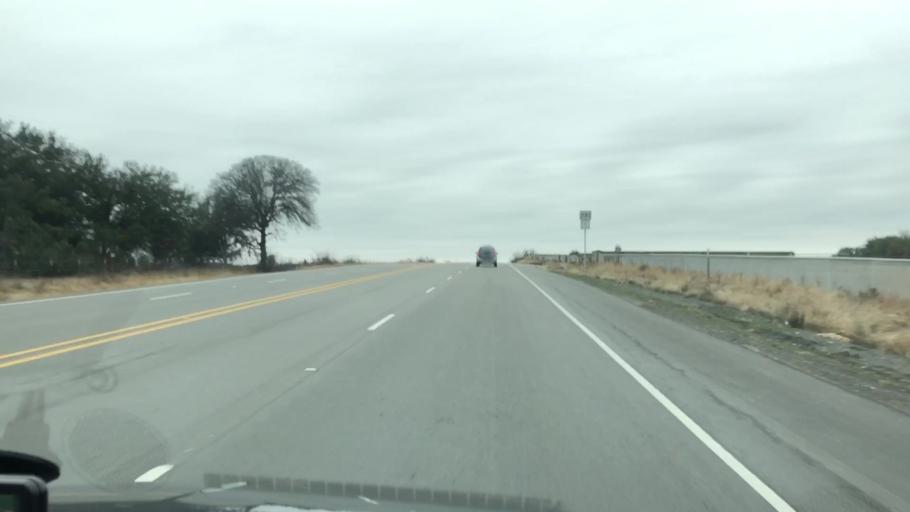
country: US
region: Texas
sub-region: Hamilton County
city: Hico
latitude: 32.0037
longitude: -98.0543
